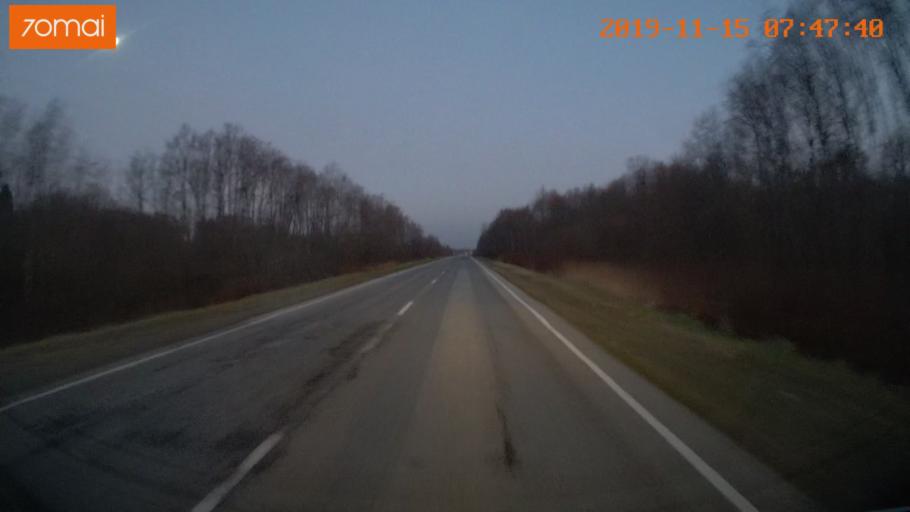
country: RU
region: Vologda
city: Sheksna
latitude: 58.8435
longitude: 38.2572
